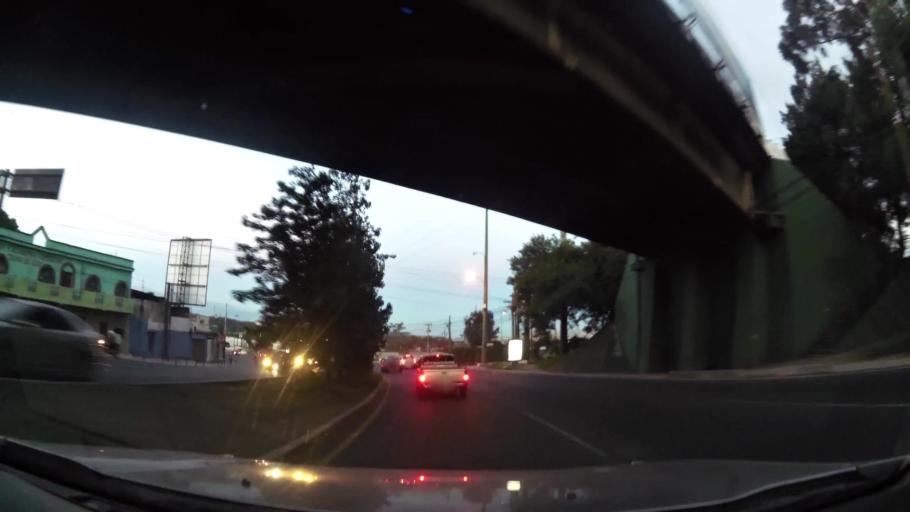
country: GT
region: Guatemala
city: Mixco
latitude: 14.6285
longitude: -90.5998
